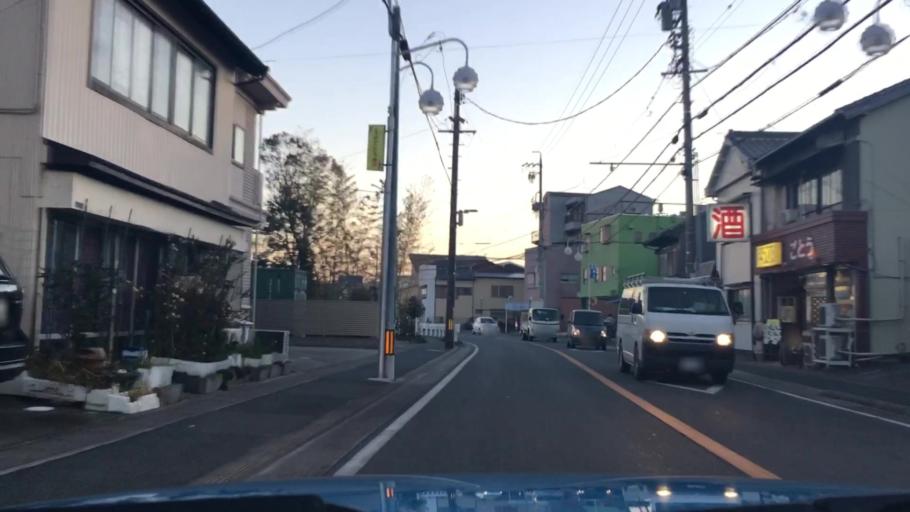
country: JP
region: Shizuoka
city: Hamamatsu
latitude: 34.7143
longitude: 137.7211
